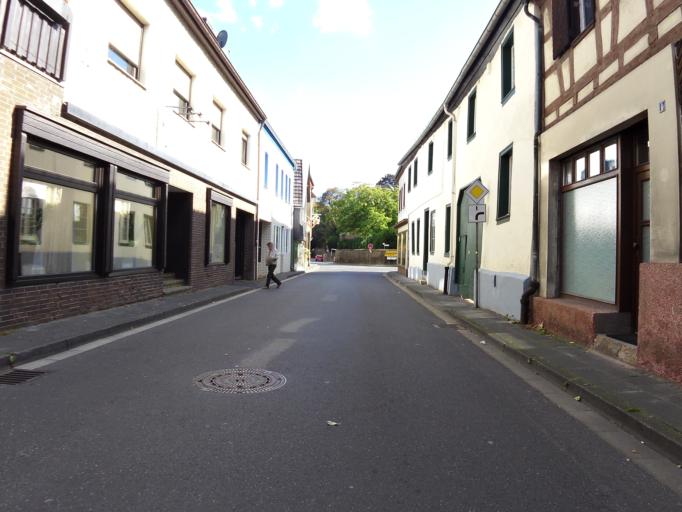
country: DE
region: North Rhine-Westphalia
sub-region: Regierungsbezirk Koln
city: Euskirchen
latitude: 50.6244
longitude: 6.8499
